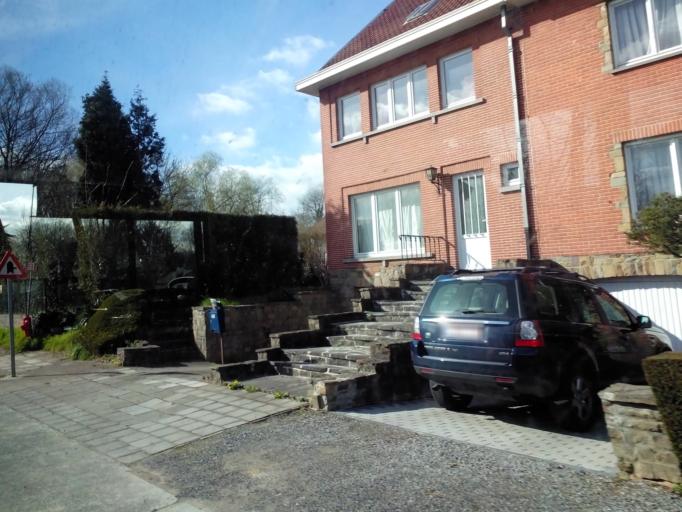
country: BE
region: Flanders
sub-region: Provincie Vlaams-Brabant
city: Kraainem
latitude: 50.8623
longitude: 4.4821
